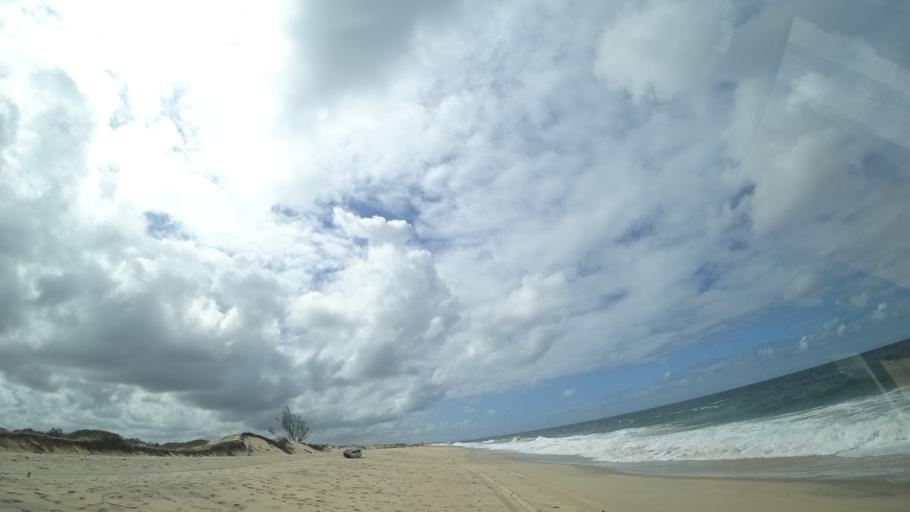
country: MZ
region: Sofala
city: Beira
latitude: -19.6177
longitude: 35.2179
